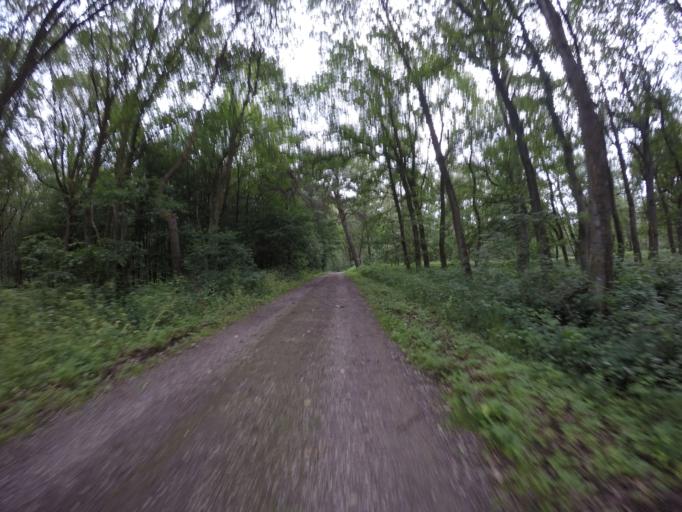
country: DE
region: North Rhine-Westphalia
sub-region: Regierungsbezirk Dusseldorf
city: Schermbeck
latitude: 51.5946
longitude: 6.8573
